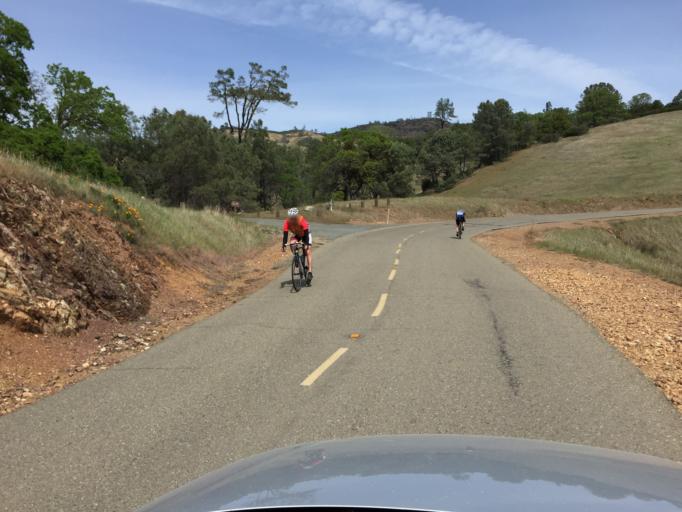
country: US
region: California
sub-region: Contra Costa County
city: Diablo
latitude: 37.8632
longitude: -121.9292
